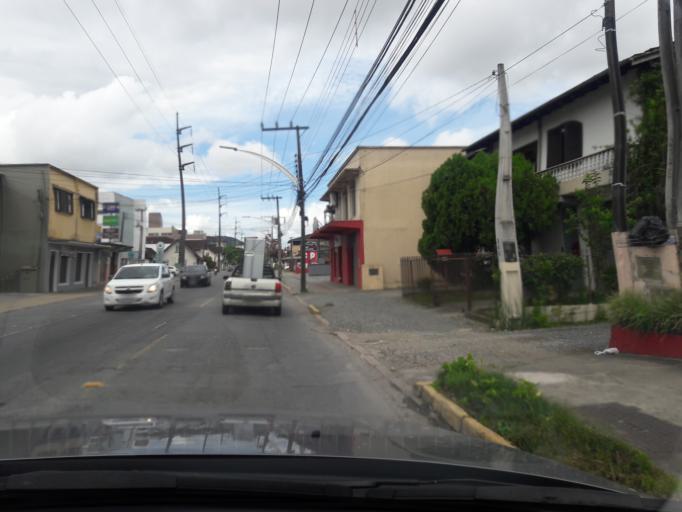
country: BR
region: Santa Catarina
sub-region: Joinville
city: Joinville
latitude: -26.3217
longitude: -48.8524
